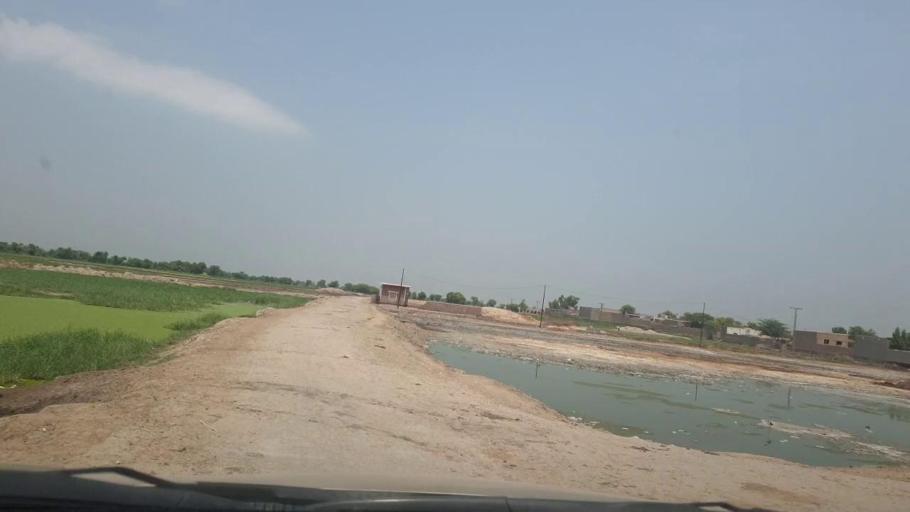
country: PK
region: Sindh
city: Ratodero
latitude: 27.7264
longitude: 68.2952
